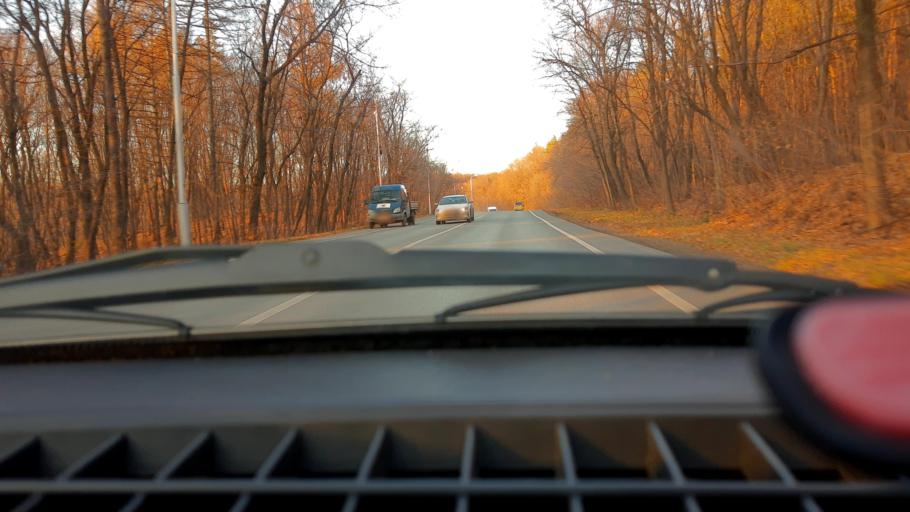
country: RU
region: Bashkortostan
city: Ufa
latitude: 54.8760
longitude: 56.0620
